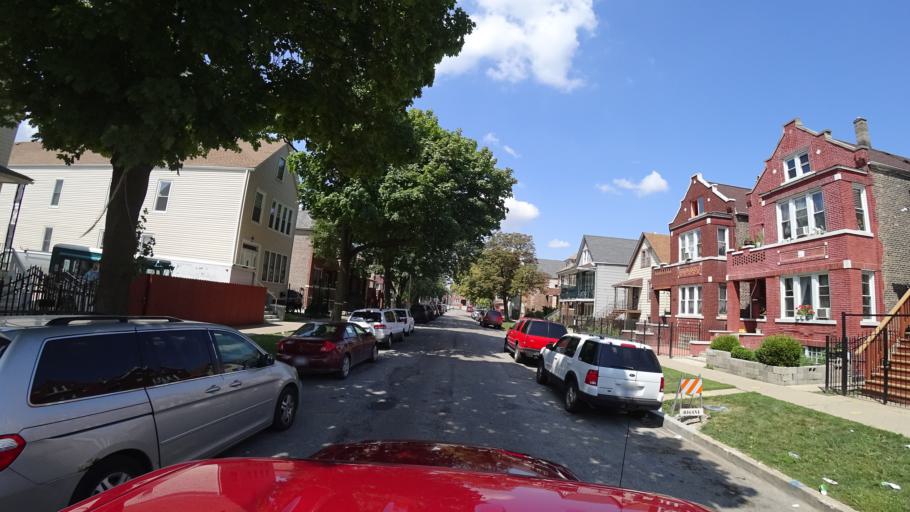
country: US
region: Illinois
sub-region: Cook County
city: Chicago
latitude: 41.8111
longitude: -87.6876
